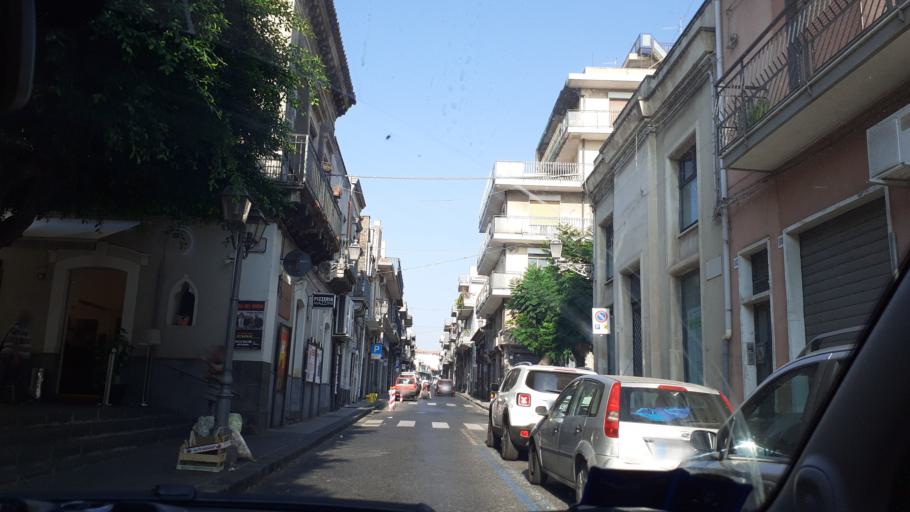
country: IT
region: Sicily
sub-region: Catania
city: Misterbianco
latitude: 37.5182
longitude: 15.0080
